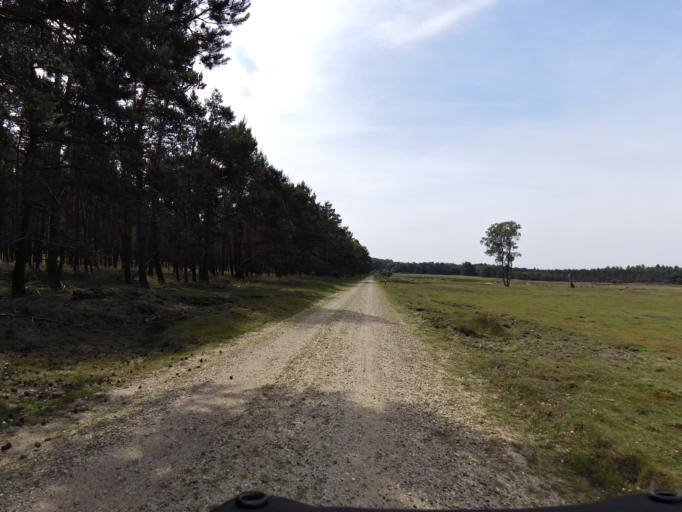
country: NL
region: Gelderland
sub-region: Gemeente Apeldoorn
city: Loenen
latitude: 52.0833
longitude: 5.9835
